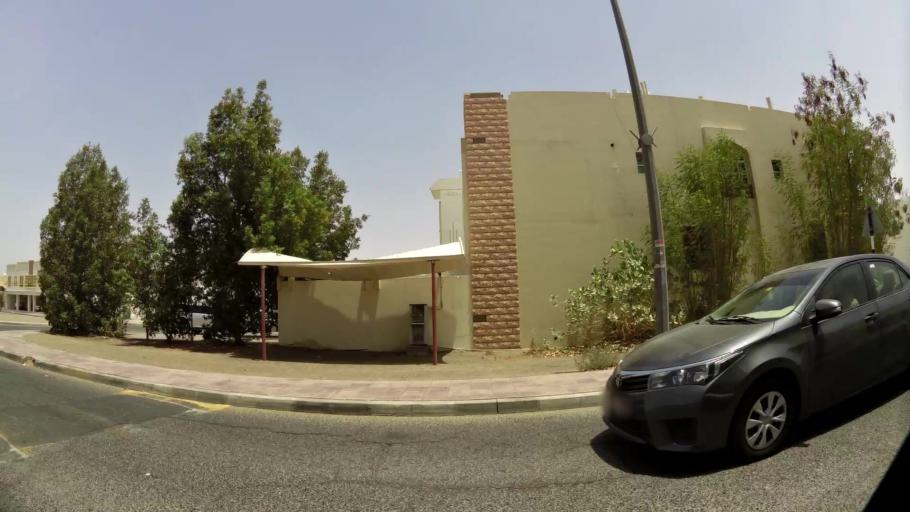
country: AE
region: Abu Dhabi
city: Al Ain
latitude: 24.2071
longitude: 55.7210
